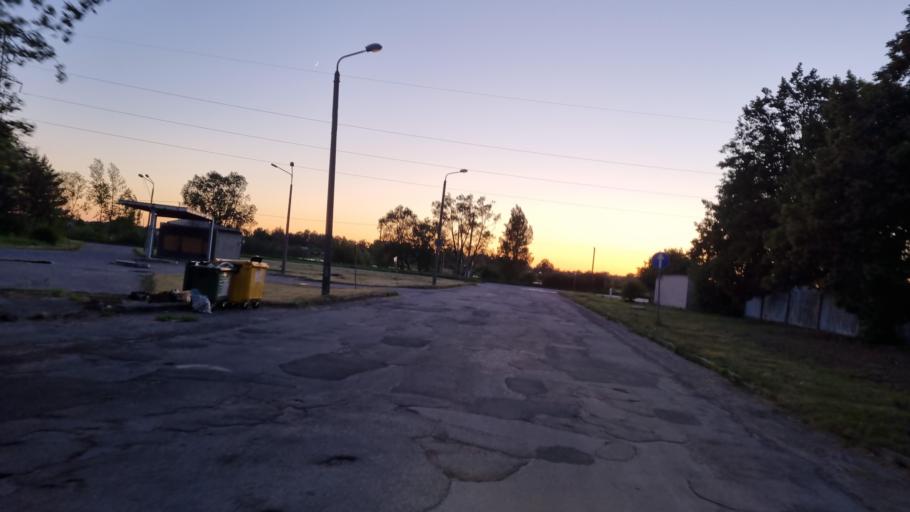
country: LV
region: Riga
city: Daugavgriva
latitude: 57.0244
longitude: 24.0265
